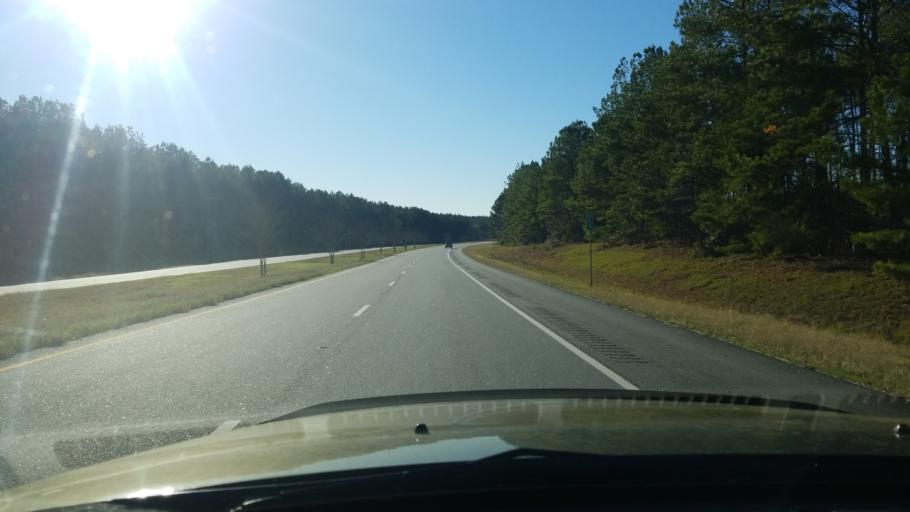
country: US
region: Georgia
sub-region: Talbot County
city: Talbotton
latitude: 32.5476
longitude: -84.7064
